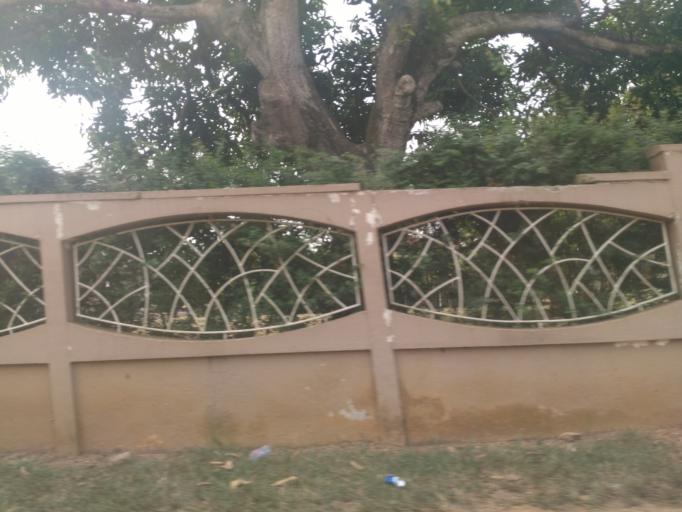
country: GH
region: Ashanti
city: Kumasi
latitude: 6.6725
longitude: -1.6172
